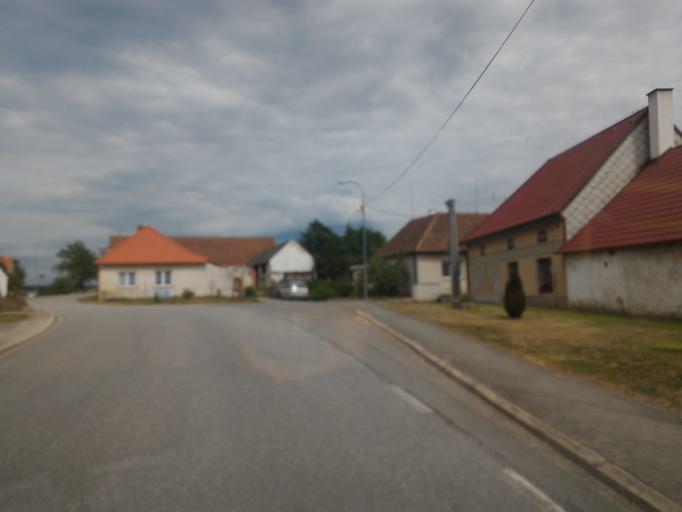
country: CZ
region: Jihocesky
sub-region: Okres Jindrichuv Hradec
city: Dacice
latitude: 49.1034
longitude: 15.4938
